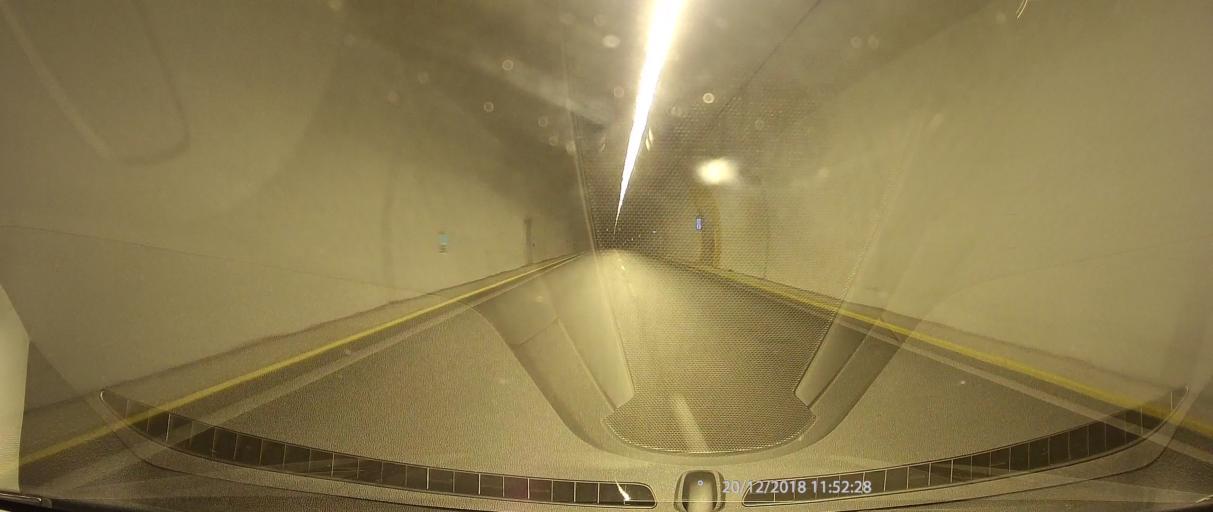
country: GR
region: West Greece
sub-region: Nomos Achaias
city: Aiyira
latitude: 38.1355
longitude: 22.3879
